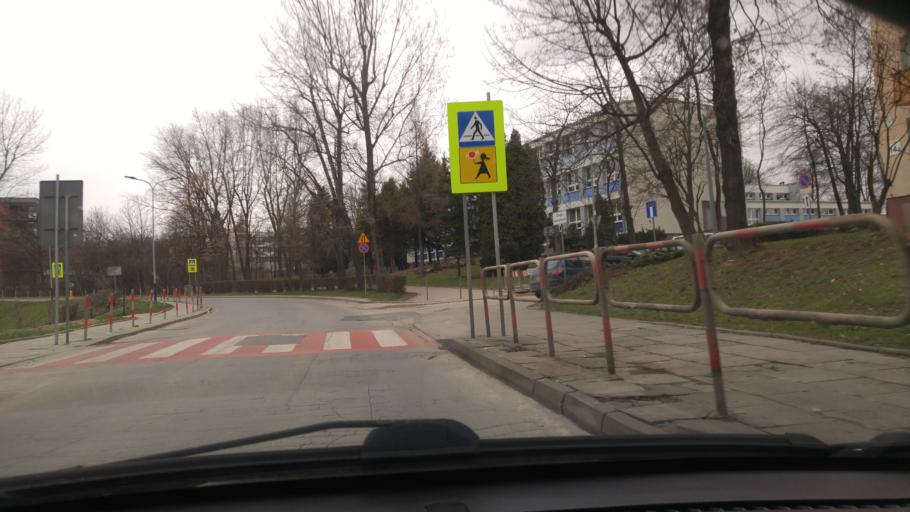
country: PL
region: Lesser Poland Voivodeship
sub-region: Powiat wielicki
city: Kokotow
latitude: 50.0968
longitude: 20.0606
